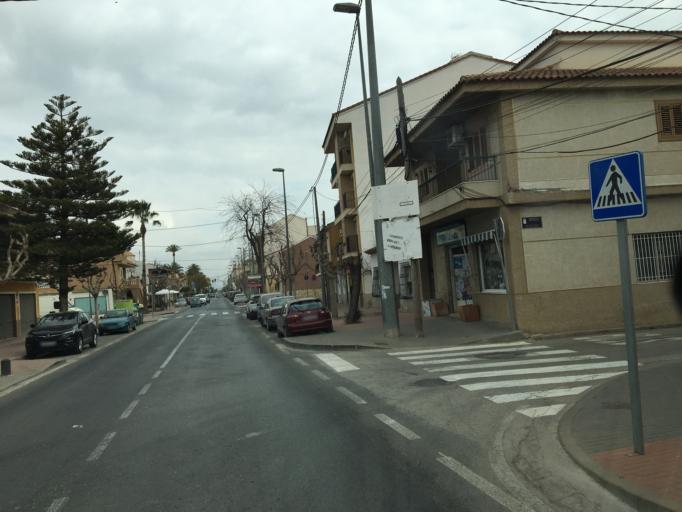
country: ES
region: Murcia
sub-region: Murcia
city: Beniel
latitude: 38.0393
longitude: -1.0294
